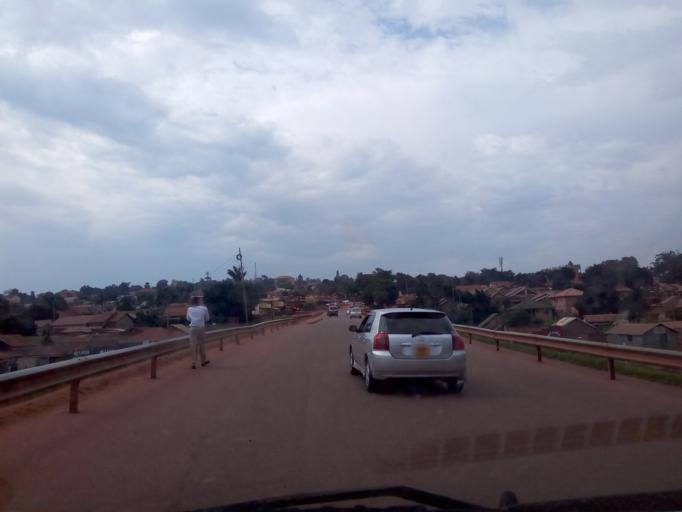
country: UG
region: Central Region
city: Kampala Central Division
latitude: 0.3499
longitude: 32.5792
